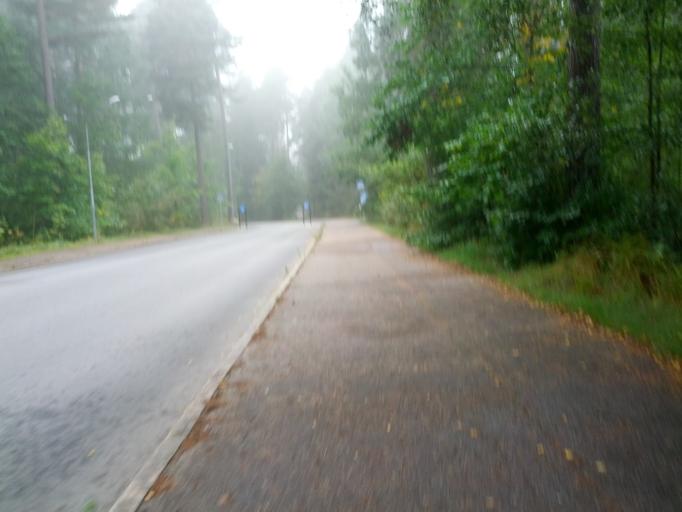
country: SE
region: Uppsala
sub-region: Uppsala Kommun
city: Uppsala
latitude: 59.8329
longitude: 17.6461
